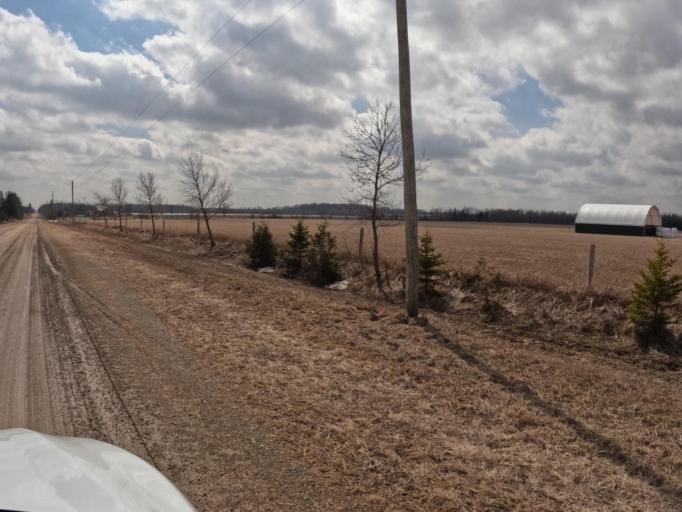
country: CA
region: Ontario
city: Shelburne
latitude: 44.0199
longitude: -80.3295
